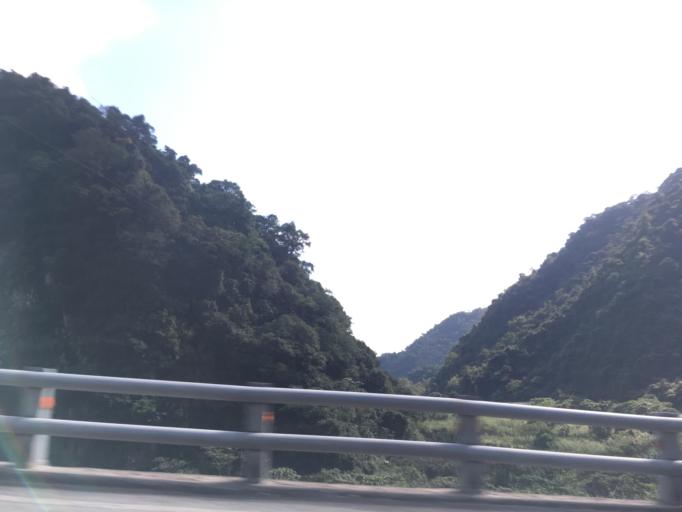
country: TW
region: Taiwan
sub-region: Yilan
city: Yilan
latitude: 24.7520
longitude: 121.6637
